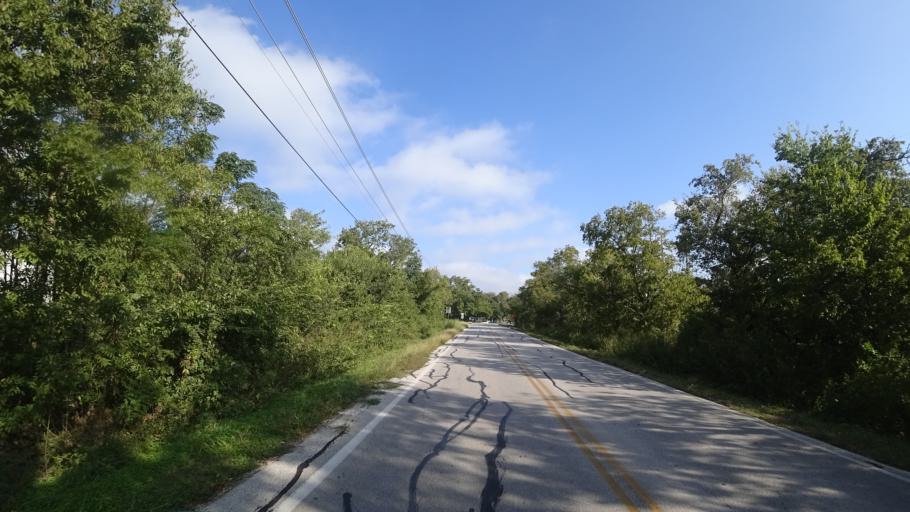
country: US
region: Texas
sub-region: Travis County
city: Manor
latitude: 30.3510
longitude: -97.6464
